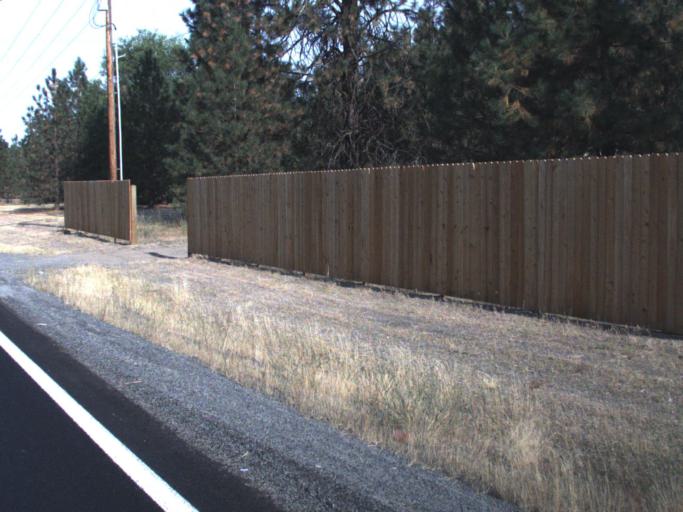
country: US
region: Washington
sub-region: Spokane County
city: Deer Park
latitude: 47.8466
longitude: -117.6293
